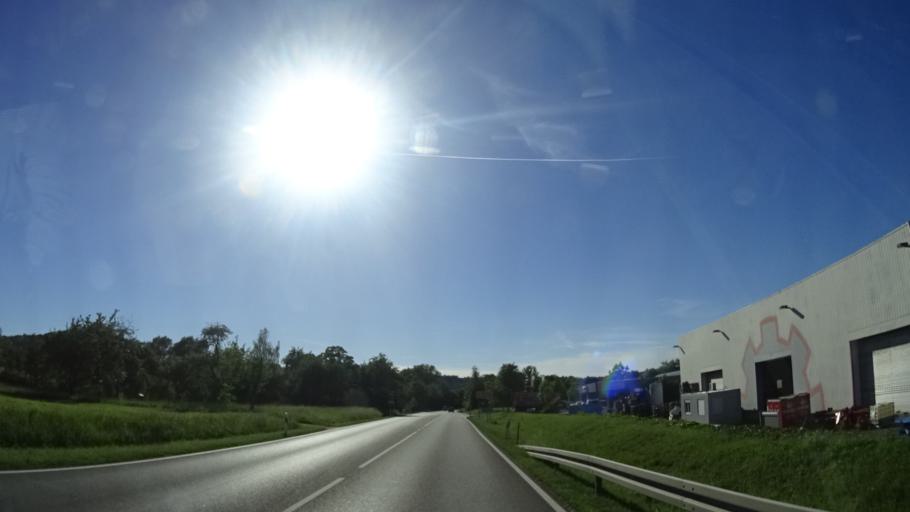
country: DE
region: Baden-Wuerttemberg
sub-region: Regierungsbezirk Stuttgart
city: Vellberg
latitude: 49.0971
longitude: 9.8308
